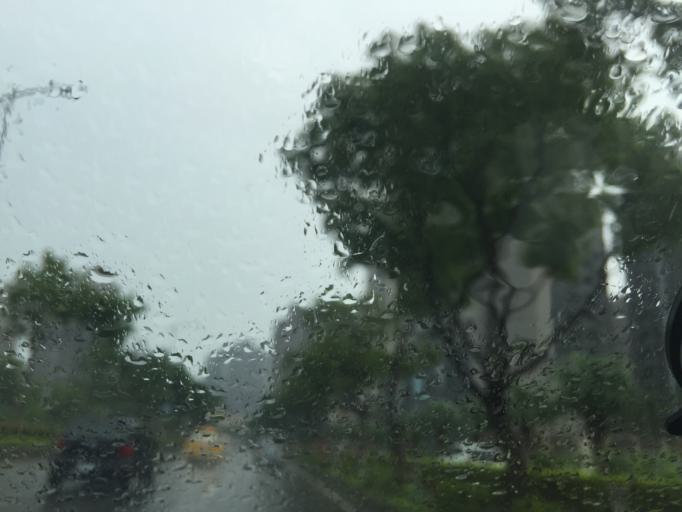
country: TW
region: Taiwan
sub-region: Hsinchu
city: Zhubei
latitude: 24.8154
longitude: 121.0320
